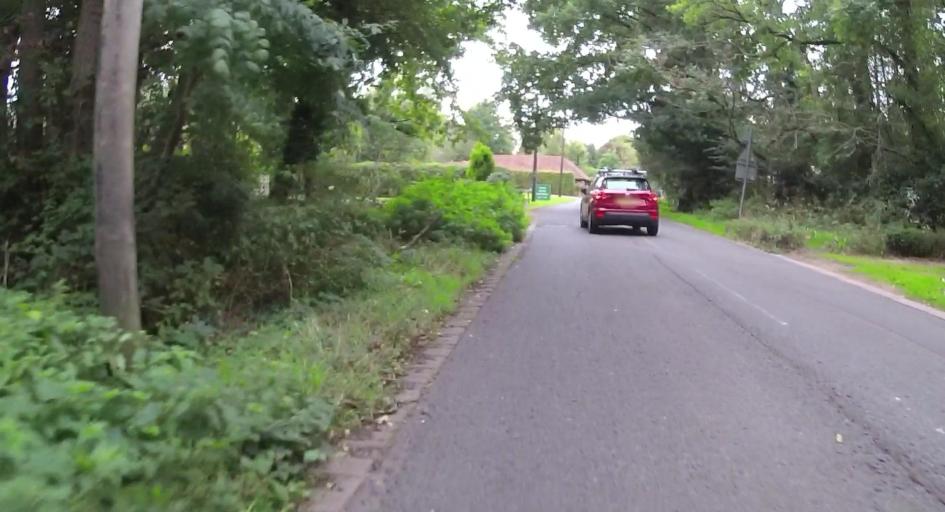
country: GB
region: England
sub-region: Surrey
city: Knaphill
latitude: 51.3334
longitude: -0.6432
